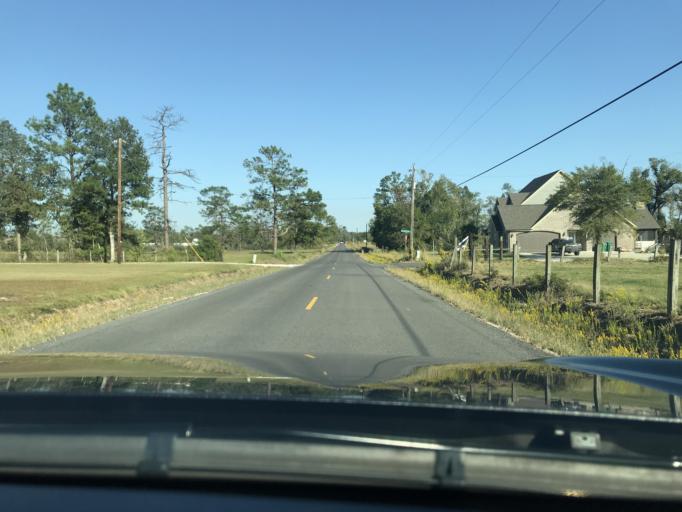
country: US
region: Louisiana
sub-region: Calcasieu Parish
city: Westlake
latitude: 30.3153
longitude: -93.2672
